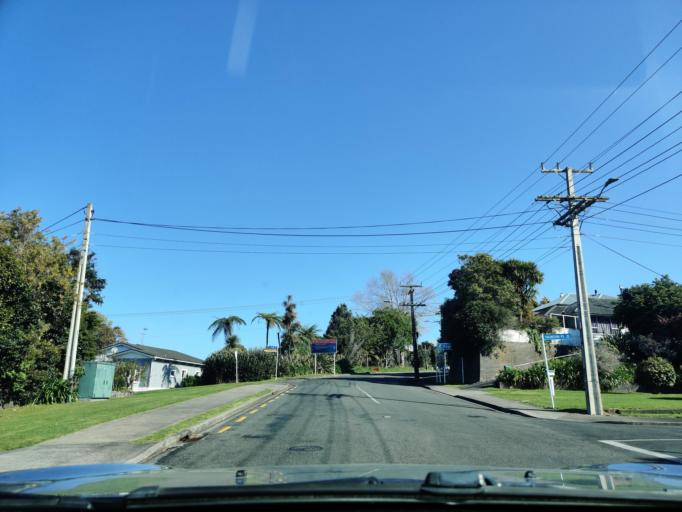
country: NZ
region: Taranaki
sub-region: New Plymouth District
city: New Plymouth
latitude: -39.0671
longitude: 174.0547
